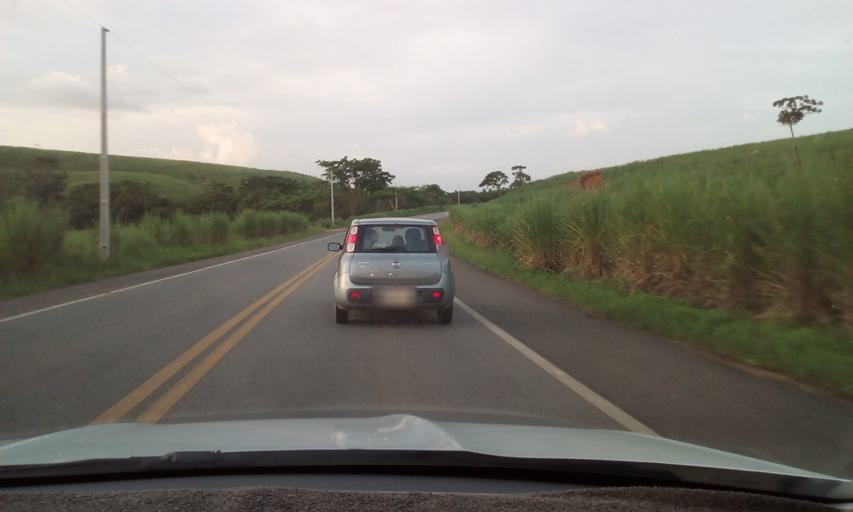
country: BR
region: Pernambuco
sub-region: Vicencia
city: Vicencia
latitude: -7.6415
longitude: -35.2546
